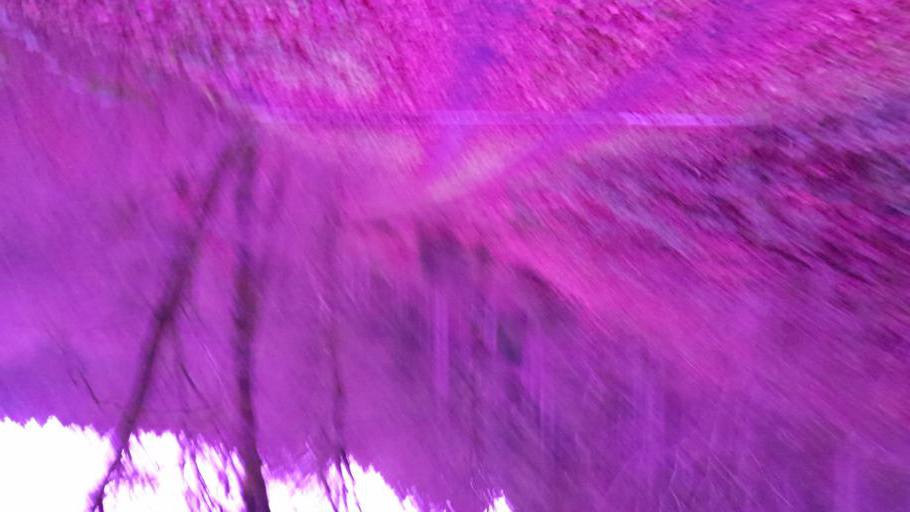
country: DE
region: Rheinland-Pfalz
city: Dasburg
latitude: 50.0820
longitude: 6.1018
